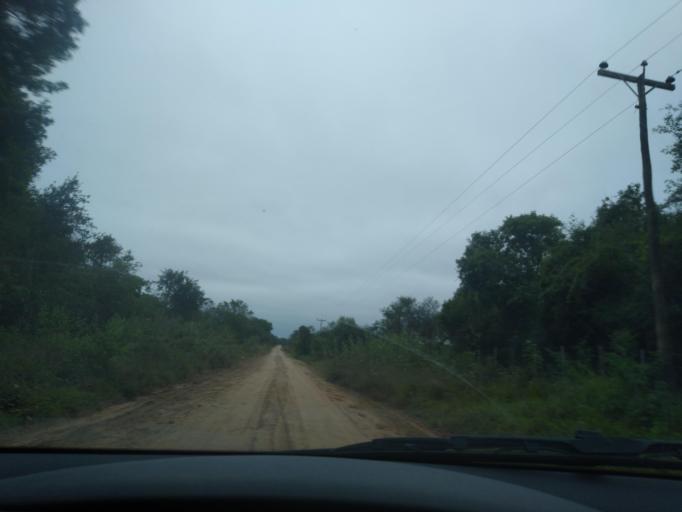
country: AR
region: Chaco
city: Colonia Benitez
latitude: -27.3537
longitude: -58.9668
